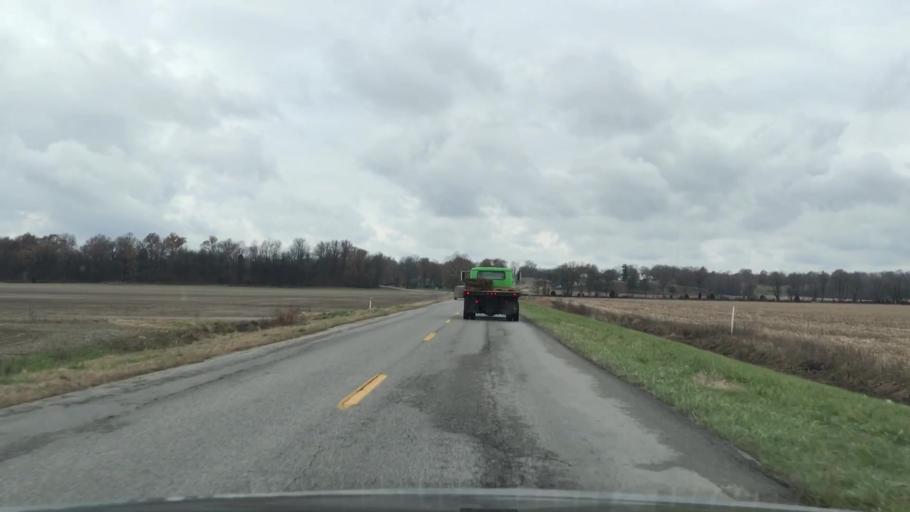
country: US
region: Kentucky
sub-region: McLean County
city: Calhoun
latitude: 37.5229
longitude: -87.3798
